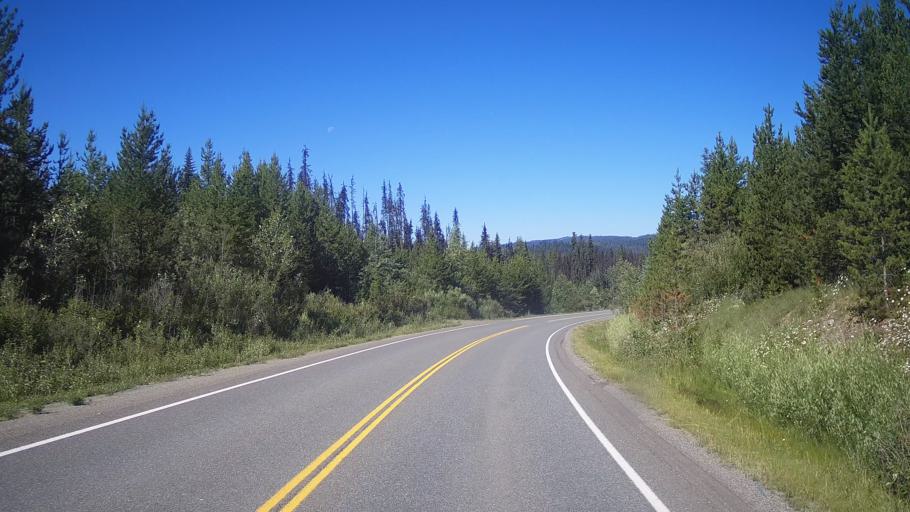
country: CA
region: British Columbia
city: Kamloops
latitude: 51.4950
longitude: -120.4075
